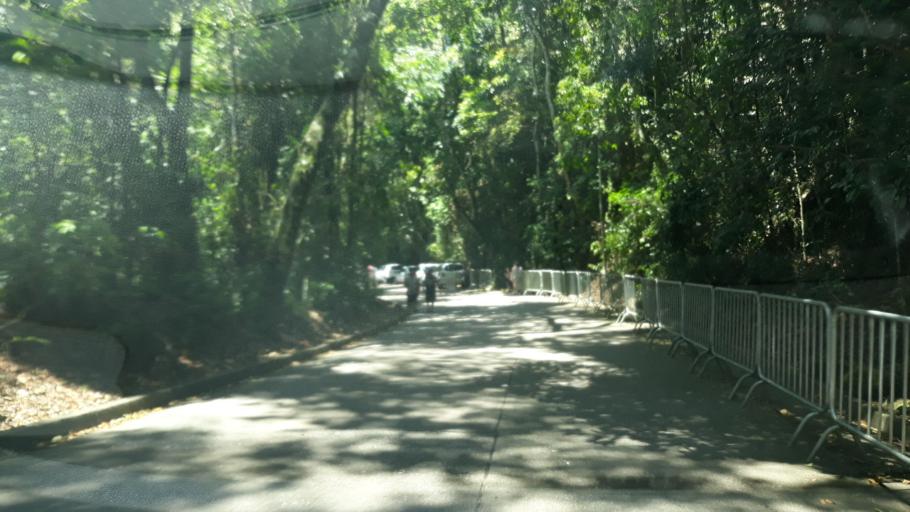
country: BR
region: Rio de Janeiro
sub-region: Rio De Janeiro
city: Rio de Janeiro
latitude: -22.9456
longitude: -43.2156
